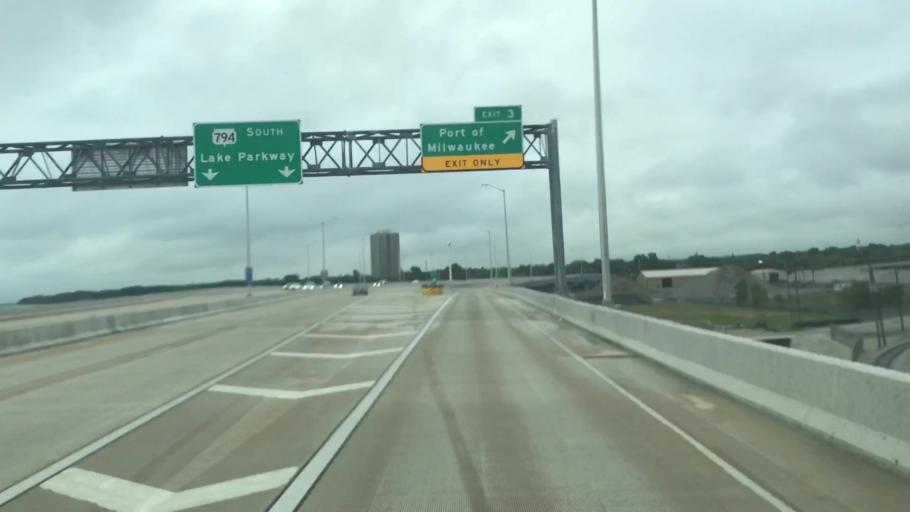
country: US
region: Wisconsin
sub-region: Milwaukee County
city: Milwaukee
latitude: 43.0090
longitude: -87.8928
